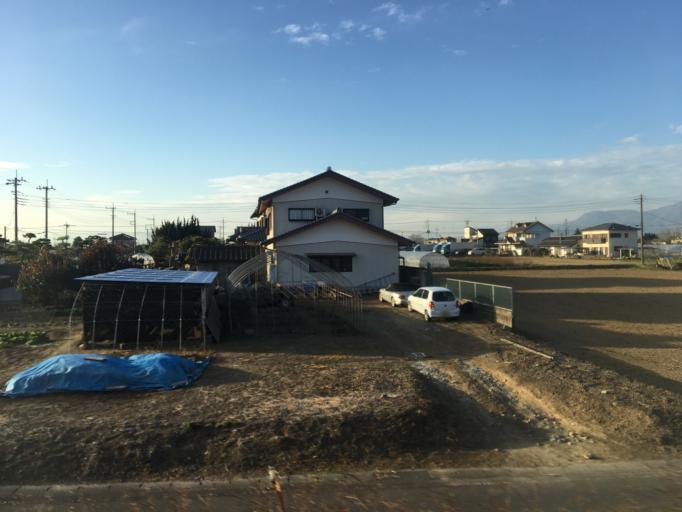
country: JP
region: Gunma
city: Isesaki
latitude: 36.3461
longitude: 139.2272
